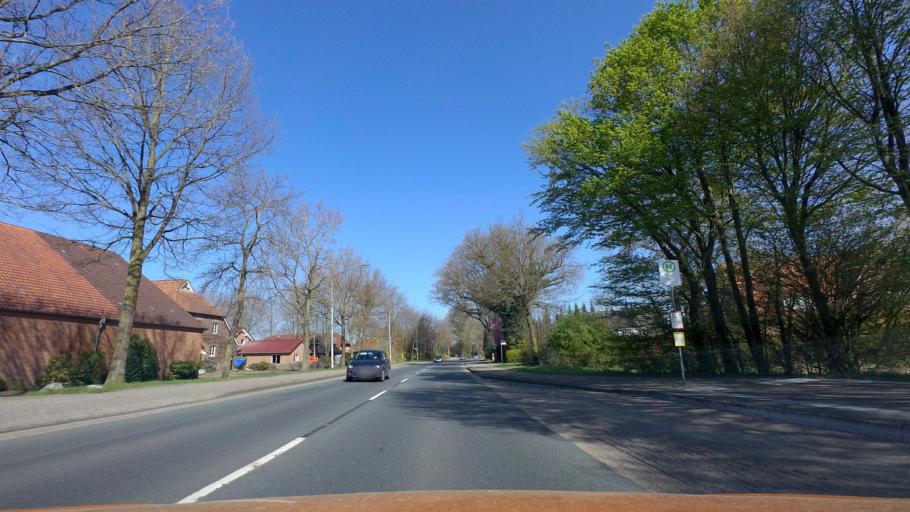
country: DE
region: Lower Saxony
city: Wardenburg
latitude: 53.0873
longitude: 8.1929
